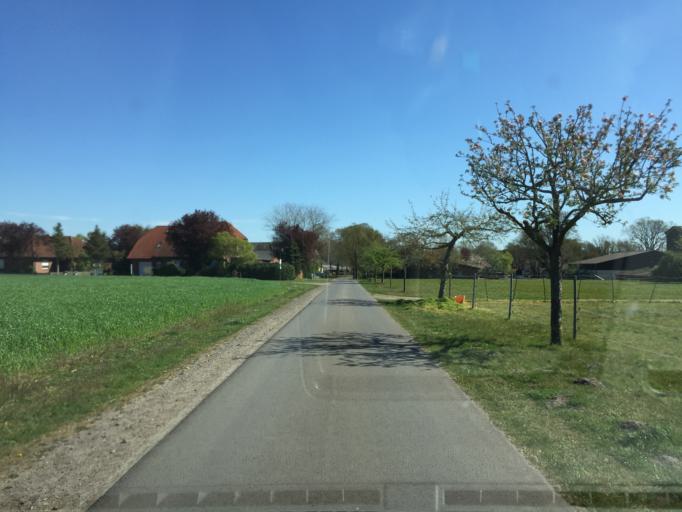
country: DE
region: Lower Saxony
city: Varrel
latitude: 52.6533
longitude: 8.7428
